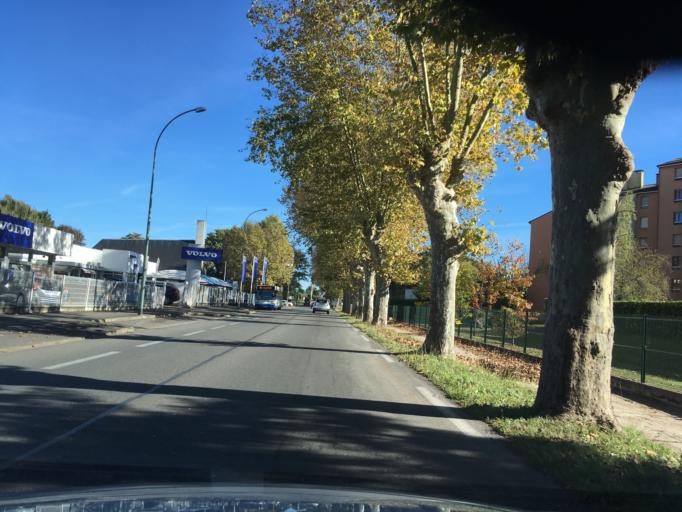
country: FR
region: Aquitaine
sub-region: Departement des Pyrenees-Atlantiques
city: Bizanos
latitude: 43.3075
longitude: -0.3371
